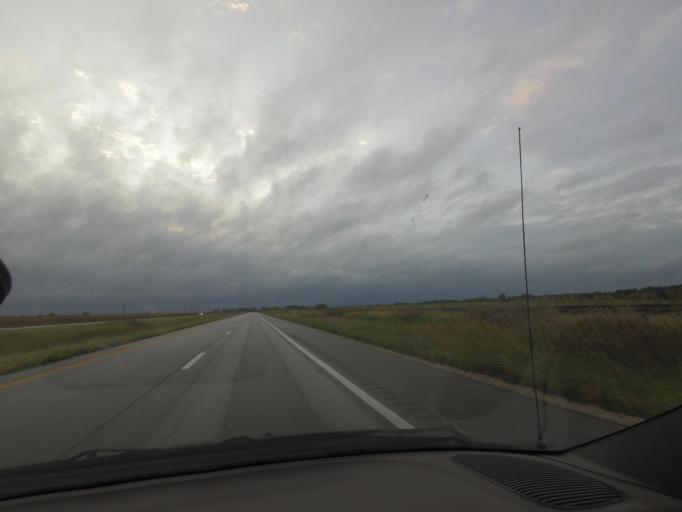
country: US
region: Missouri
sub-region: Shelby County
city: Shelbina
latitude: 39.6769
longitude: -91.9685
